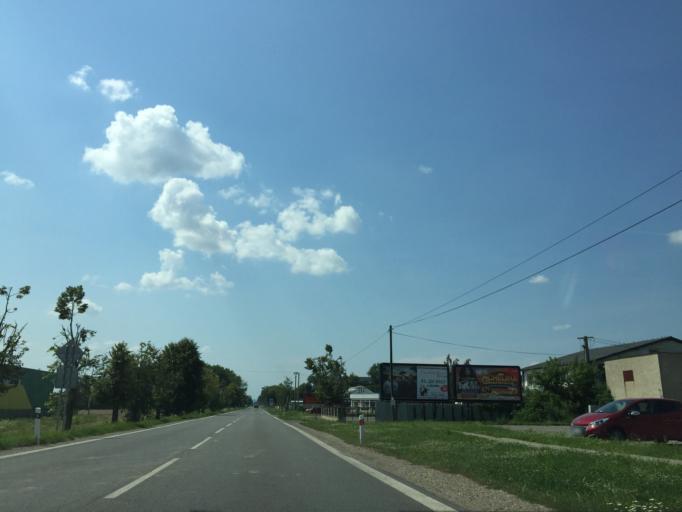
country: SK
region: Kosicky
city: Sobrance
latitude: 48.7482
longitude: 22.1719
